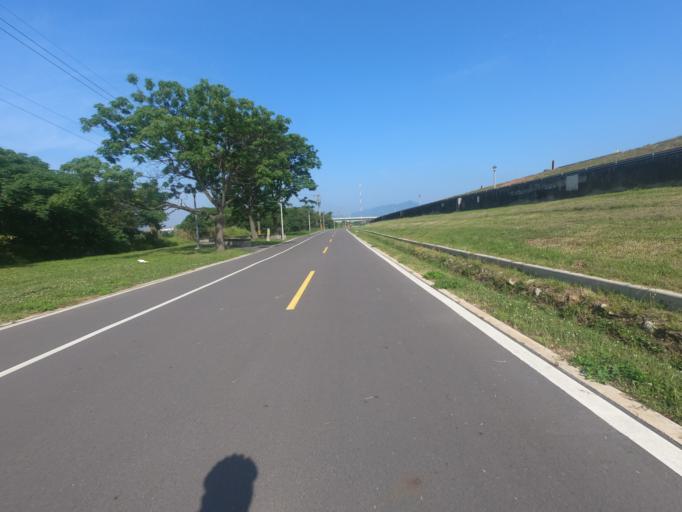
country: TW
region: Taipei
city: Taipei
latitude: 25.0973
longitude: 121.5041
